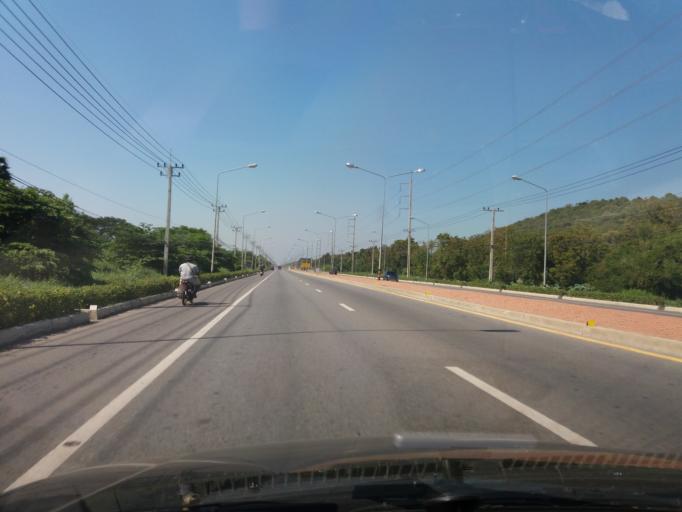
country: TH
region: Chai Nat
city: Chai Nat
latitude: 15.2024
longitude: 100.1226
